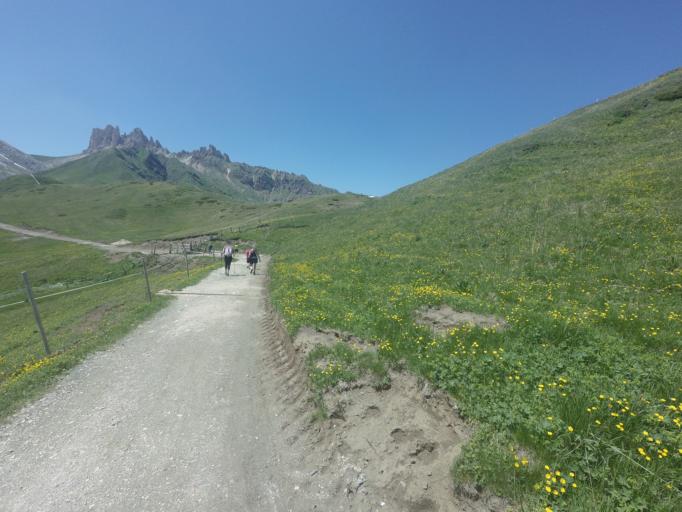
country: IT
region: Trentino-Alto Adige
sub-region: Provincia di Trento
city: Mazzin
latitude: 46.4977
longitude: 11.6576
